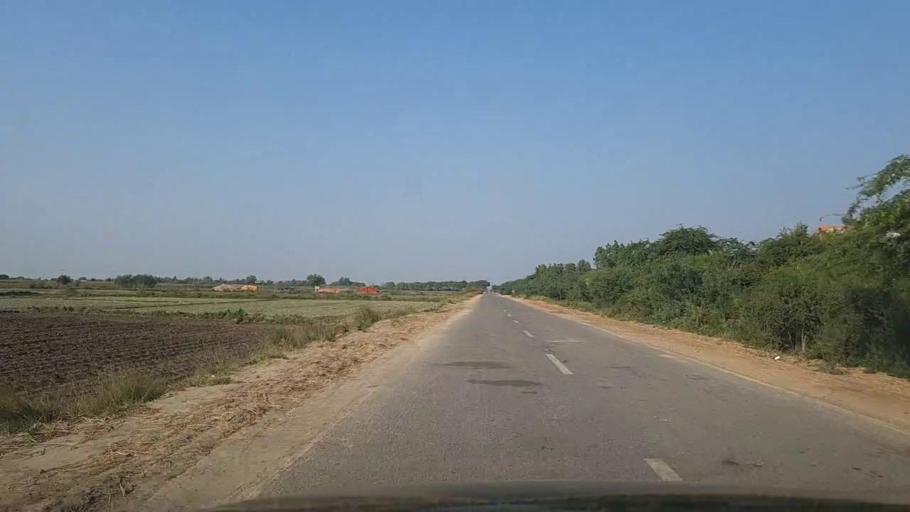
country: PK
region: Sindh
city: Thatta
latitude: 24.6171
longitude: 68.0515
